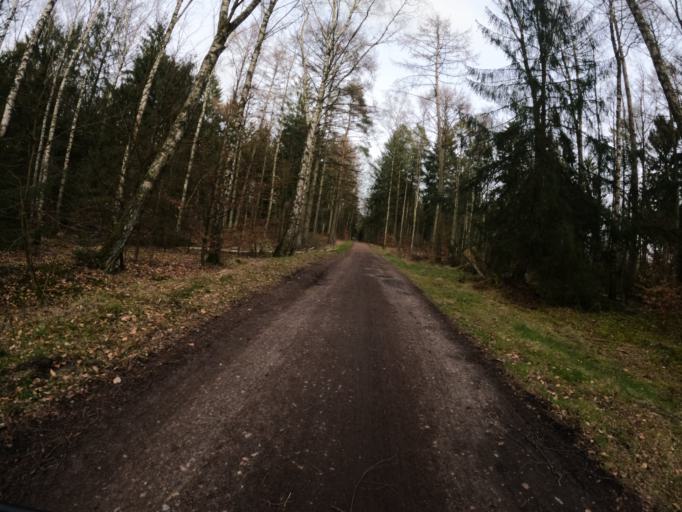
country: DE
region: Schleswig-Holstein
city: Appen
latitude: 53.6128
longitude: 9.7444
